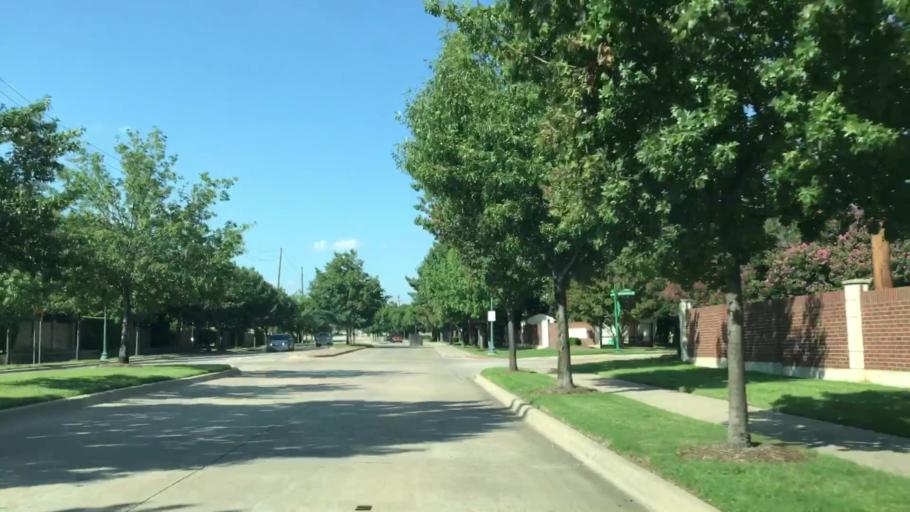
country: US
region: Texas
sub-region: Tarrant County
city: Keller
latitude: 32.9301
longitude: -97.2192
